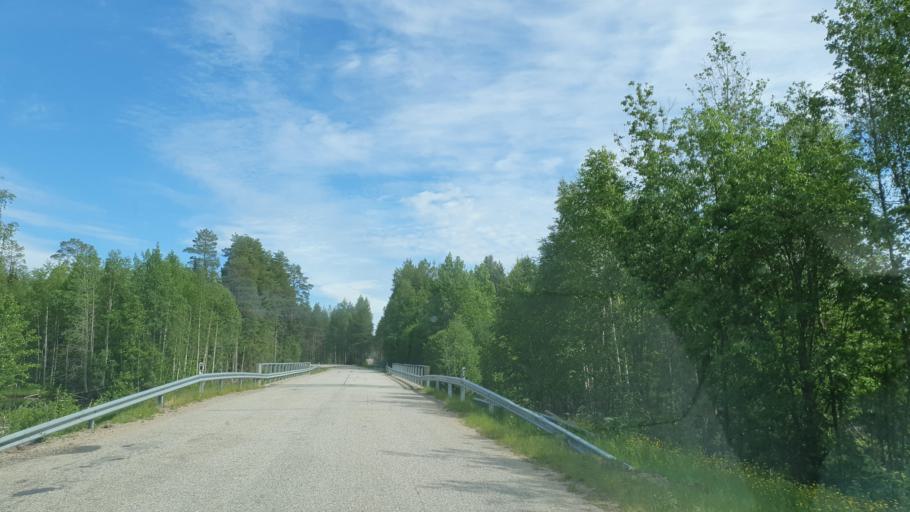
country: FI
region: Kainuu
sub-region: Kehys-Kainuu
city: Hyrynsalmi
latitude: 64.6936
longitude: 28.4811
